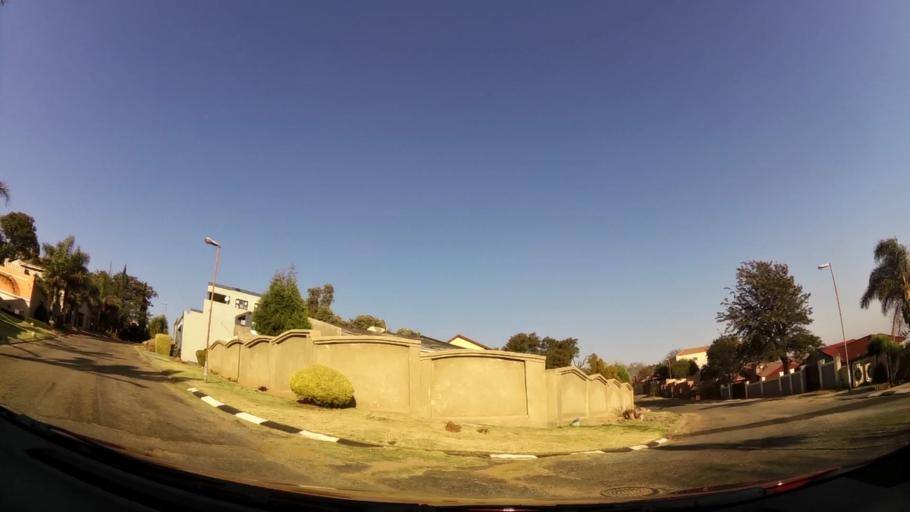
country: ZA
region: Gauteng
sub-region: City of Johannesburg Metropolitan Municipality
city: Soweto
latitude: -26.2827
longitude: 27.9603
